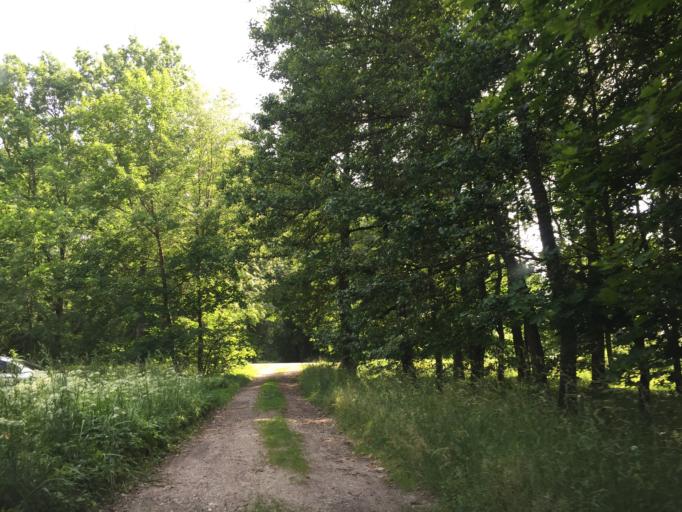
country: LV
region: Jelgava
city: Jelgava
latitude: 56.6845
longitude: 23.7213
